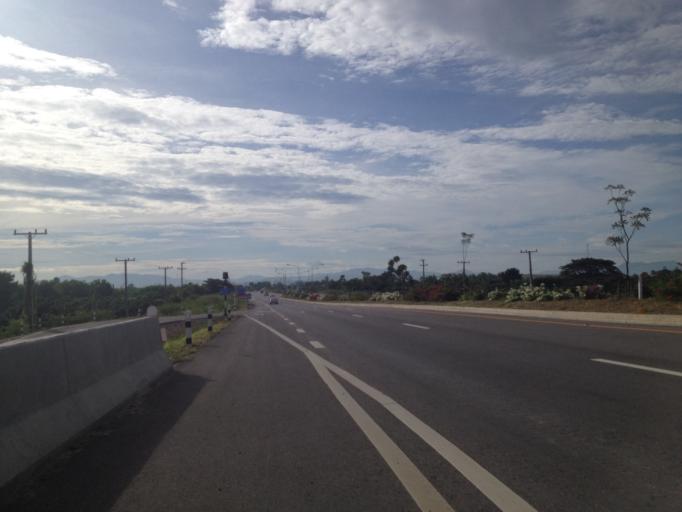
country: TH
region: Lamphun
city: Pa Sang
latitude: 18.5355
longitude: 98.8590
